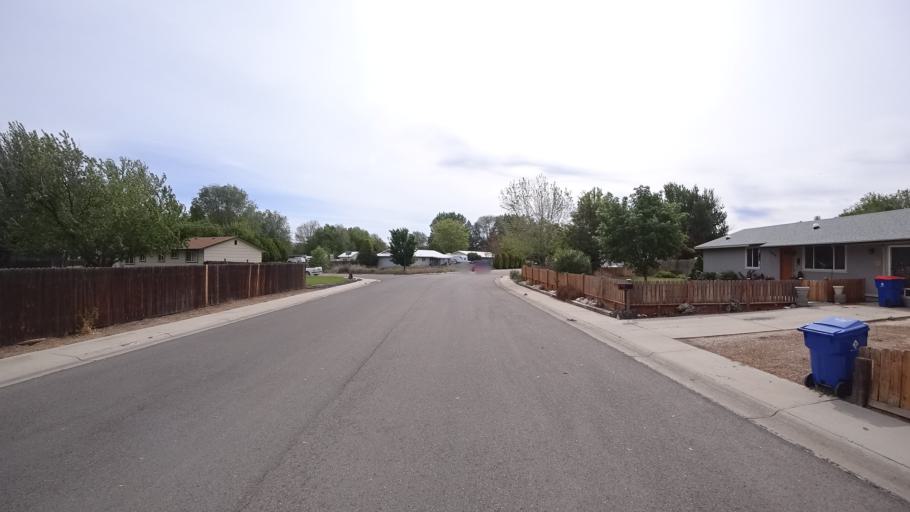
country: US
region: Idaho
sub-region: Ada County
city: Meridian
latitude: 43.5366
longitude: -116.3126
